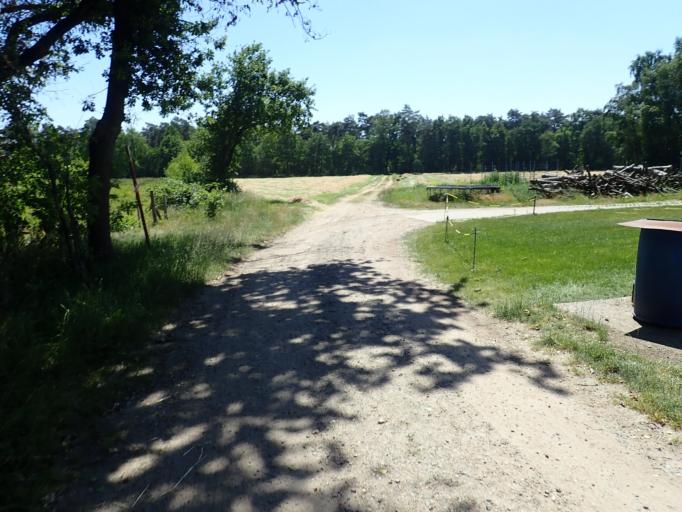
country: BE
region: Flanders
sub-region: Provincie Antwerpen
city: Beerse
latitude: 51.2915
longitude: 4.8231
